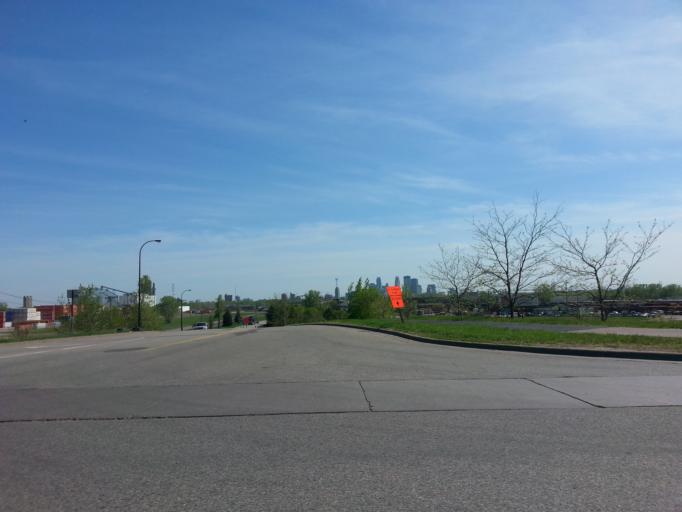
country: US
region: Minnesota
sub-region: Anoka County
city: Columbia Heights
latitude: 45.0276
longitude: -93.2631
